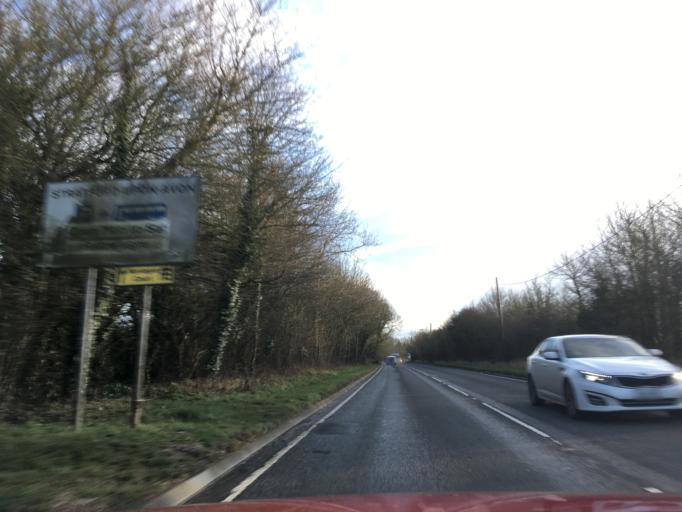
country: GB
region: England
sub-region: Warwickshire
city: Stratford-upon-Avon
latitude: 52.2148
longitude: -1.7277
